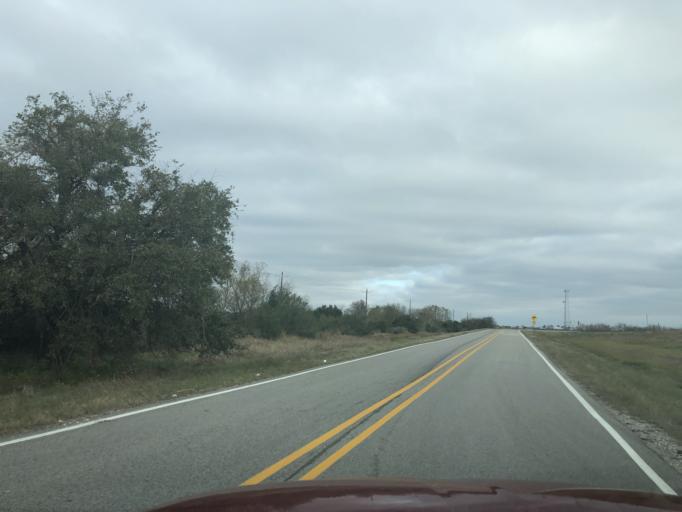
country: US
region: Texas
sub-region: Chambers County
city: Winnie
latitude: 29.8306
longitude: -94.4827
